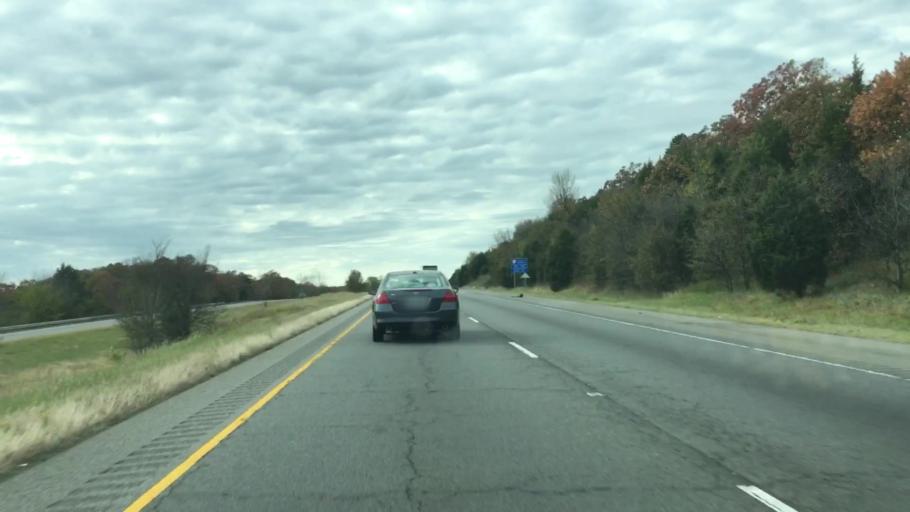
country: US
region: Arkansas
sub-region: Faulkner County
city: Conway
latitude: 35.1222
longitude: -92.4963
